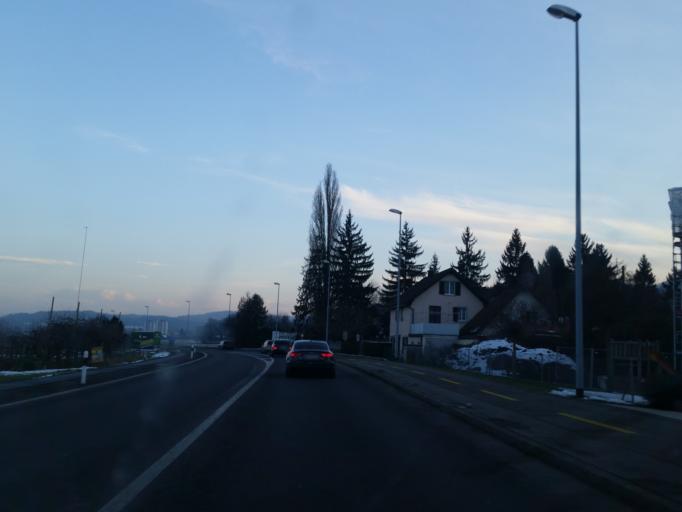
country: CH
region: Aargau
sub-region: Bezirk Baden
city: Spreitenbach
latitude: 47.4167
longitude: 8.3759
